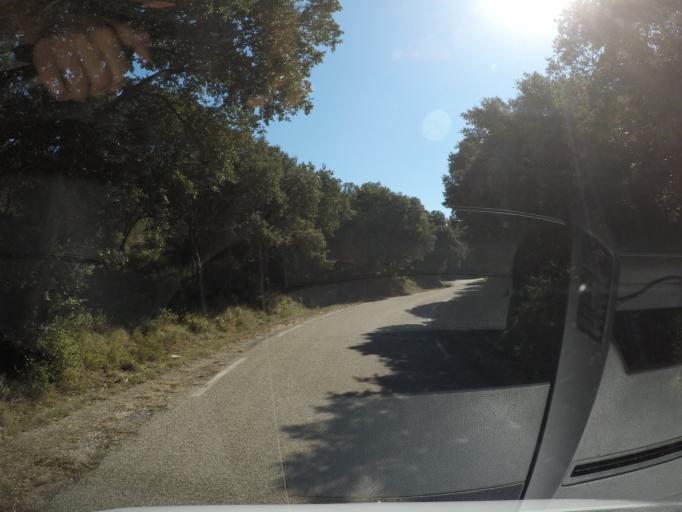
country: FR
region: Languedoc-Roussillon
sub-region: Departement du Gard
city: Saint-Victor-la-Coste
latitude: 44.0130
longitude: 4.5988
